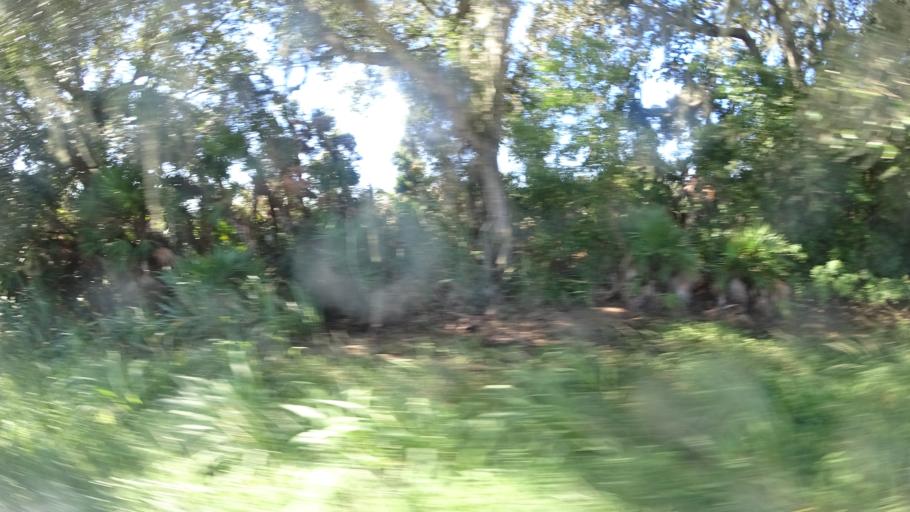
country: US
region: Florida
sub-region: Hillsborough County
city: Sun City Center
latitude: 27.6652
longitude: -82.3343
